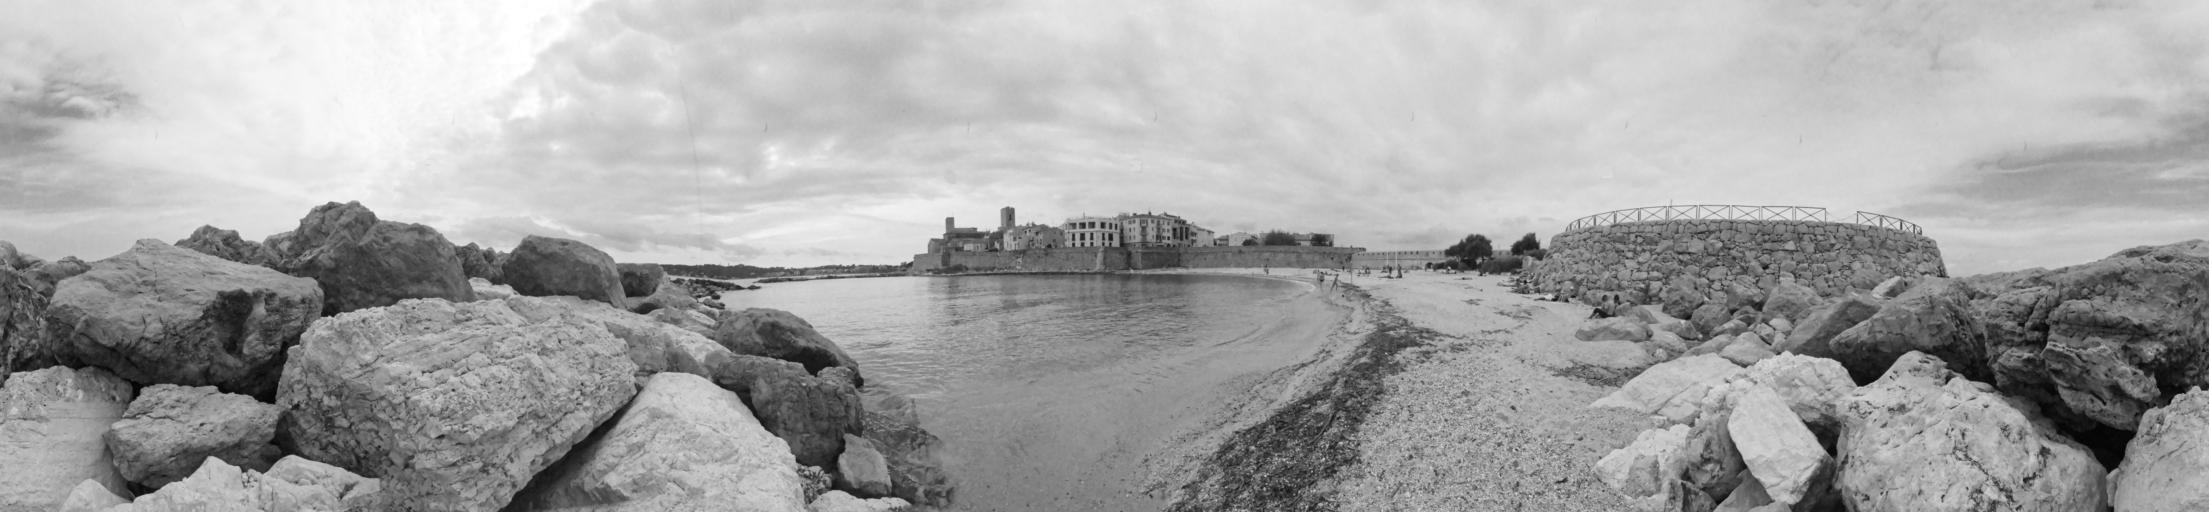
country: FR
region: Provence-Alpes-Cote d'Azur
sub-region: Departement des Alpes-Maritimes
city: Antibes
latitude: 43.5828
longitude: 7.1301
